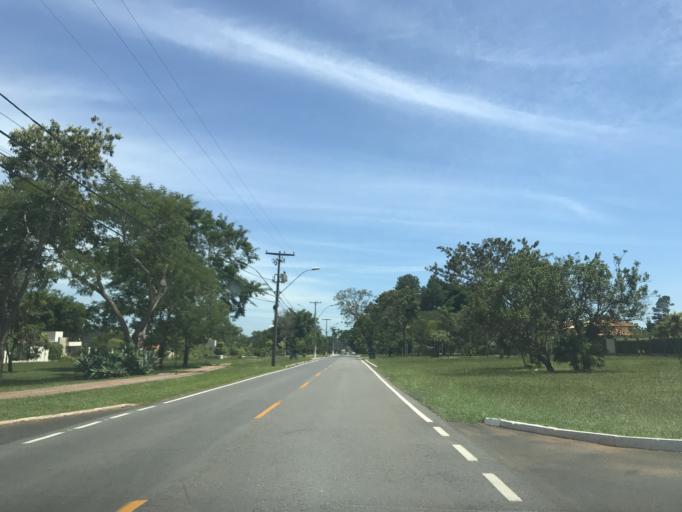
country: BR
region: Federal District
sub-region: Brasilia
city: Brasilia
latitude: -15.9027
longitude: -47.9332
